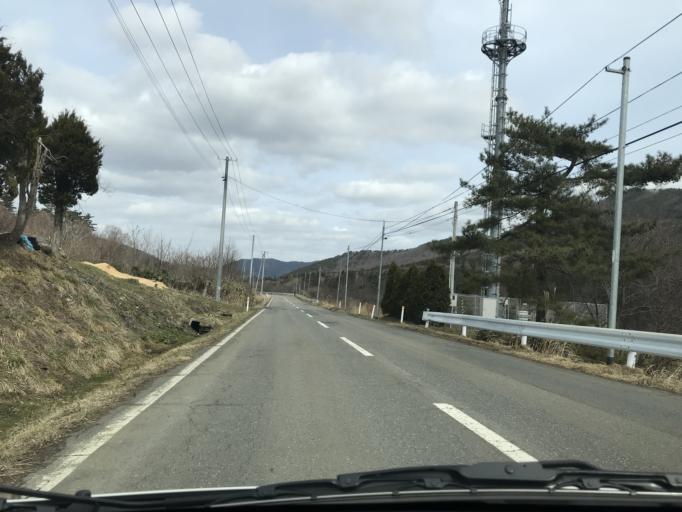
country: JP
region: Iwate
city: Kitakami
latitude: 39.2670
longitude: 141.3210
